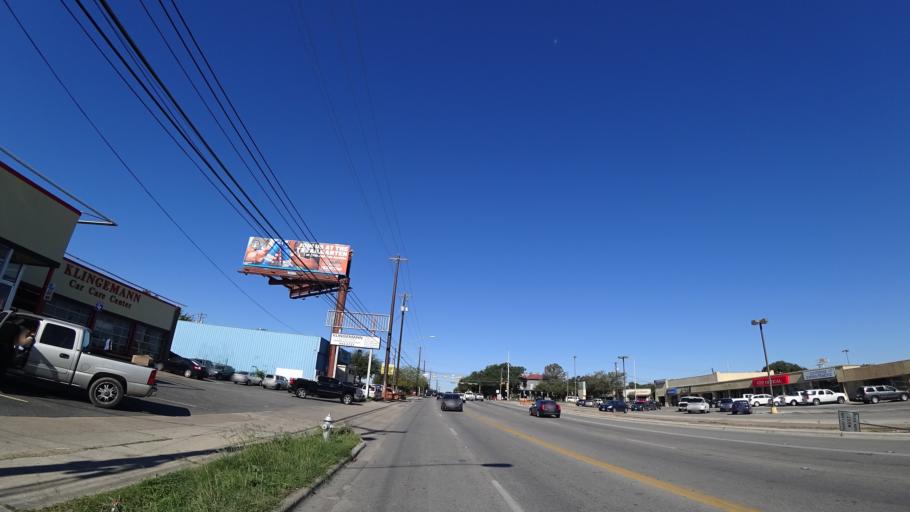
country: US
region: Texas
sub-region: Travis County
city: Austin
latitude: 30.2382
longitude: -97.7526
